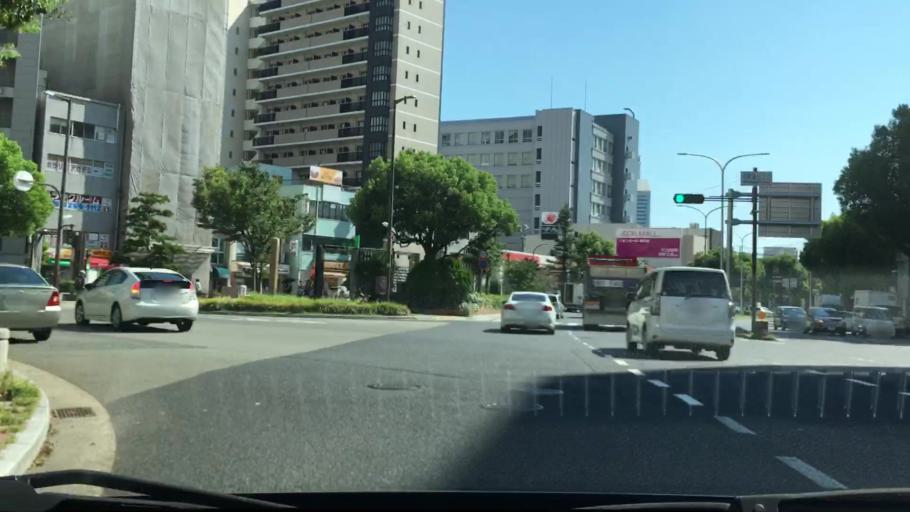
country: JP
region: Hyogo
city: Kobe
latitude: 34.6833
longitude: 135.1796
